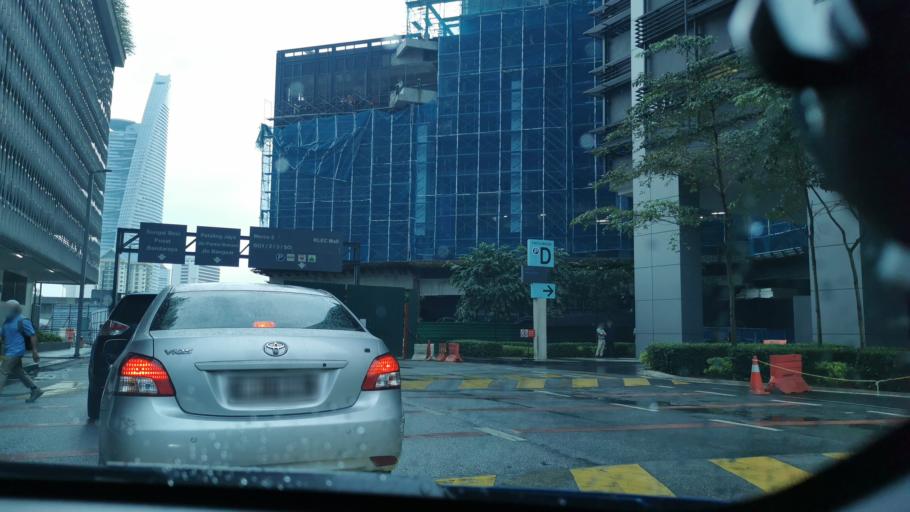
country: MY
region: Kuala Lumpur
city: Kuala Lumpur
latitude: 3.1170
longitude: 101.6739
